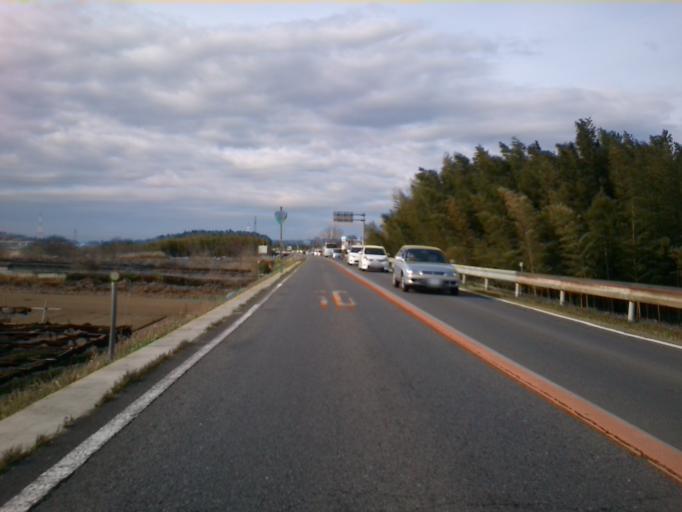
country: JP
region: Kyoto
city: Tanabe
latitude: 34.7806
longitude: 135.8065
